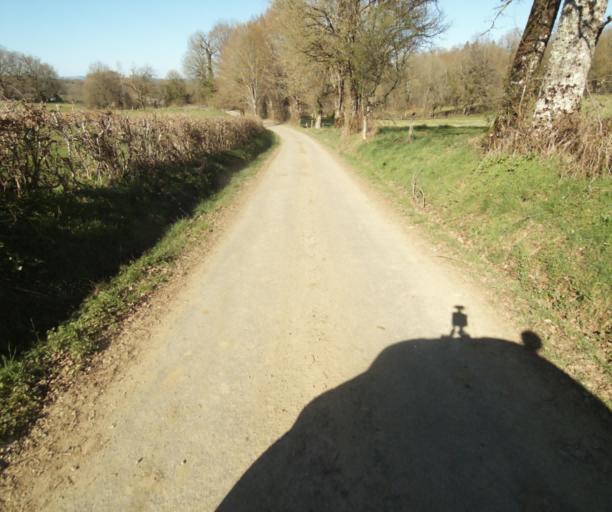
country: FR
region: Limousin
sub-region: Departement de la Correze
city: Chamboulive
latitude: 45.4318
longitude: 1.6504
